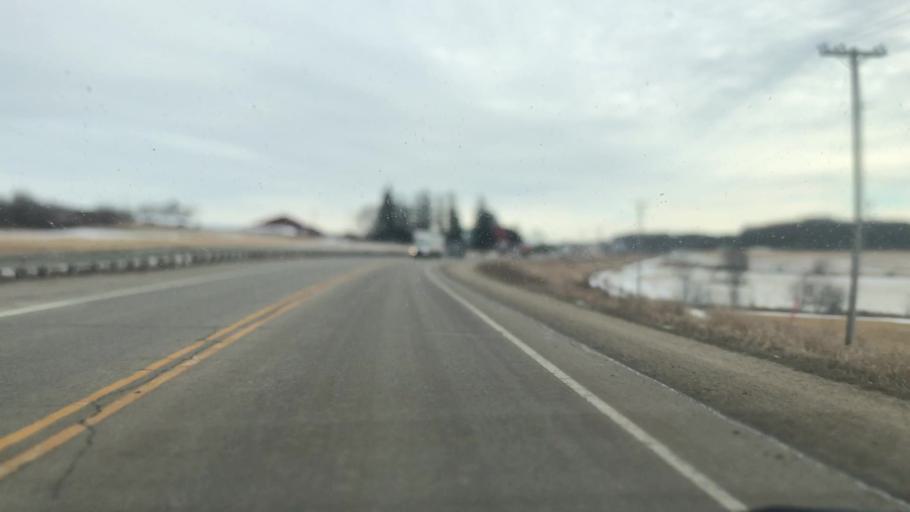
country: US
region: Wisconsin
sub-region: Dodge County
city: Mayville
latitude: 43.4428
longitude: -88.4943
